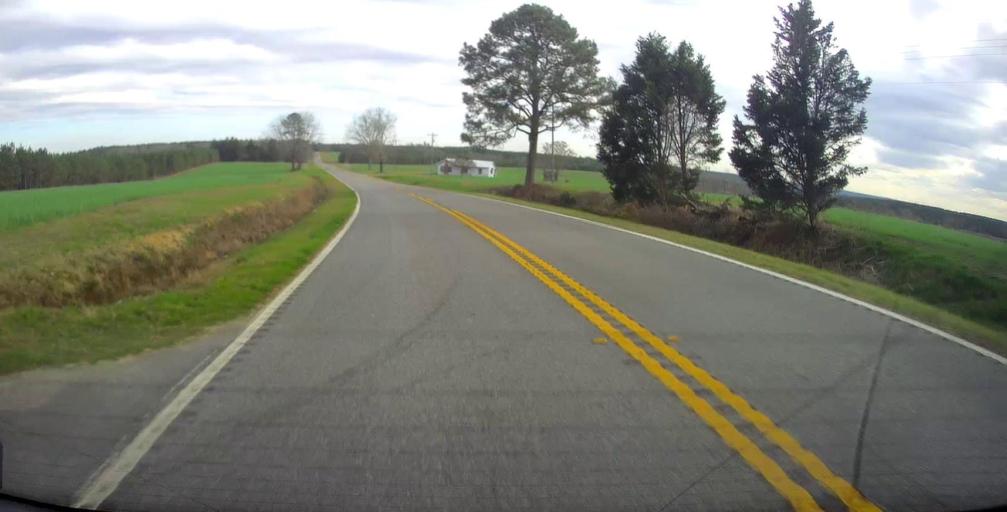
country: US
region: Georgia
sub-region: Marion County
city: Buena Vista
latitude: 32.4433
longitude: -84.4397
